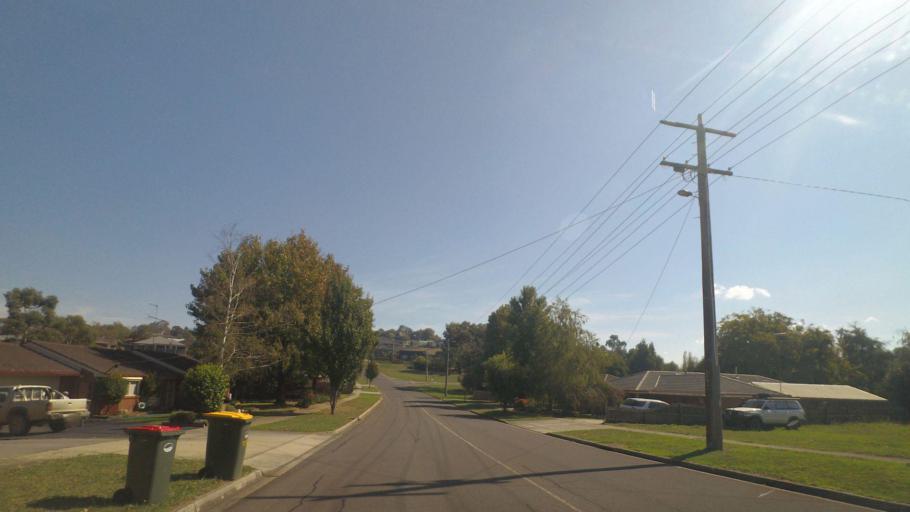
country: AU
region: Victoria
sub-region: Baw Baw
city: Warragul
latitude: -38.1434
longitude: 145.9454
